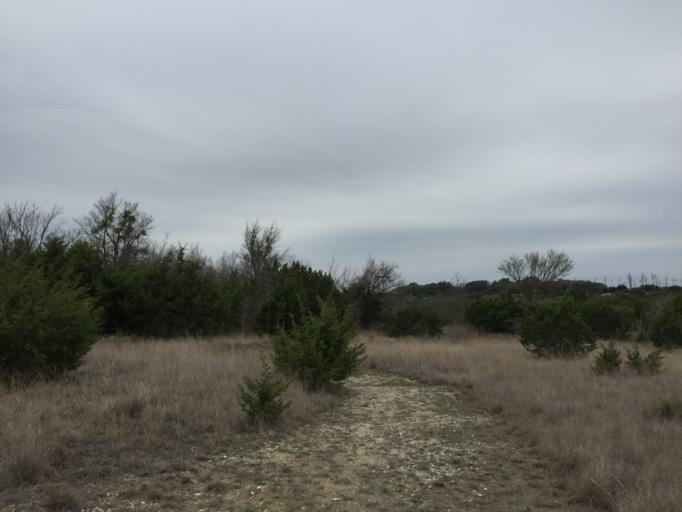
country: US
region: Texas
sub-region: Bell County
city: Fort Hood
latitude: 31.1203
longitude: -97.8147
